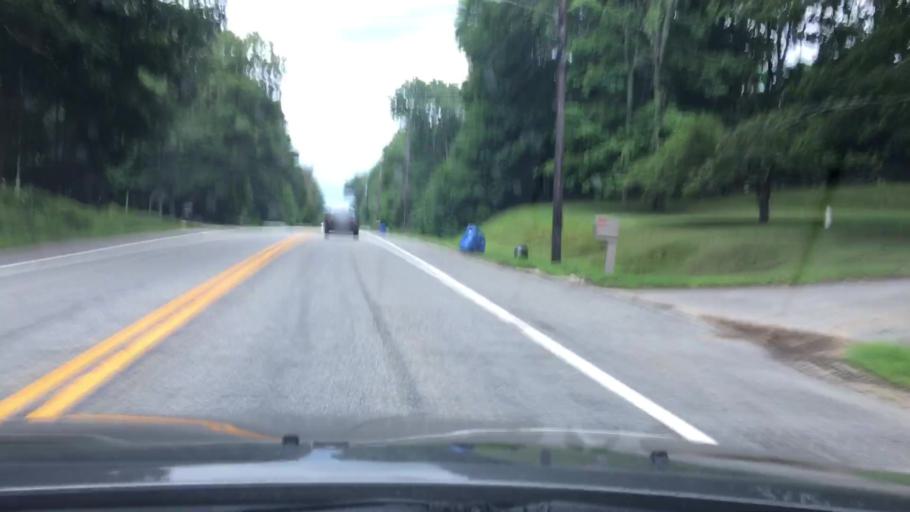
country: US
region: Rhode Island
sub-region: Providence County
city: Cumberland
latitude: 42.0089
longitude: -71.4285
